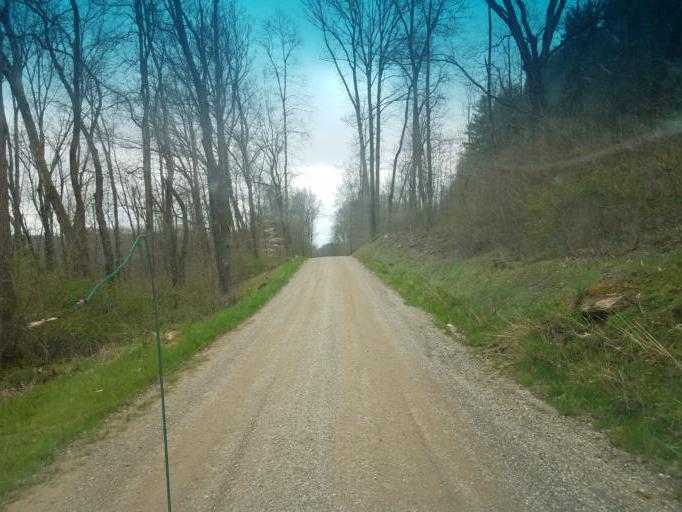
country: US
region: Ohio
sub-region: Stark County
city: Beach City
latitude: 40.6222
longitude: -81.6035
